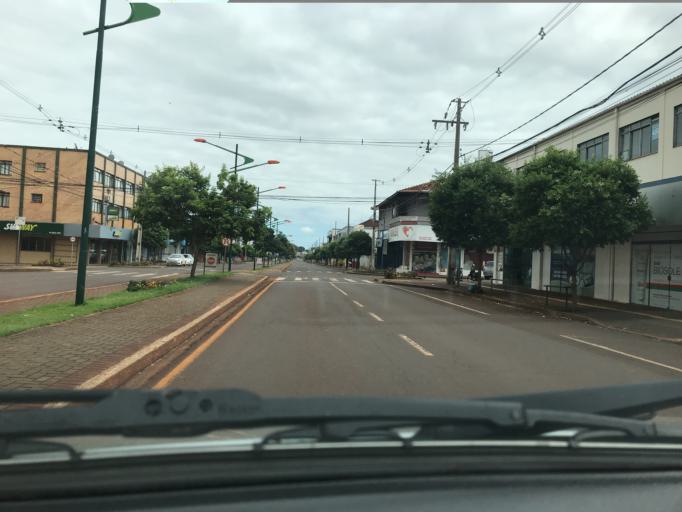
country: BR
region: Parana
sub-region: Palotina
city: Palotina
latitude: -24.2825
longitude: -53.8402
